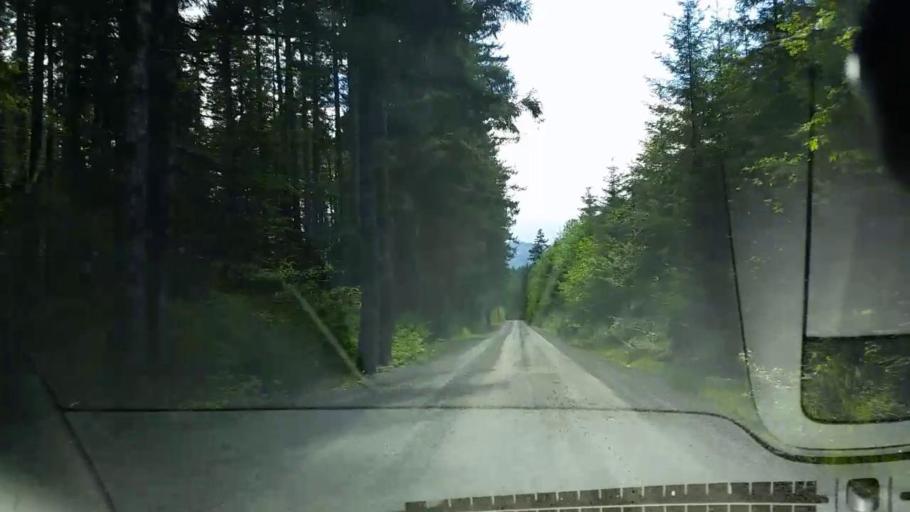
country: US
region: Washington
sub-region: Mason County
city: Shelton
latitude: 47.3563
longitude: -123.2866
